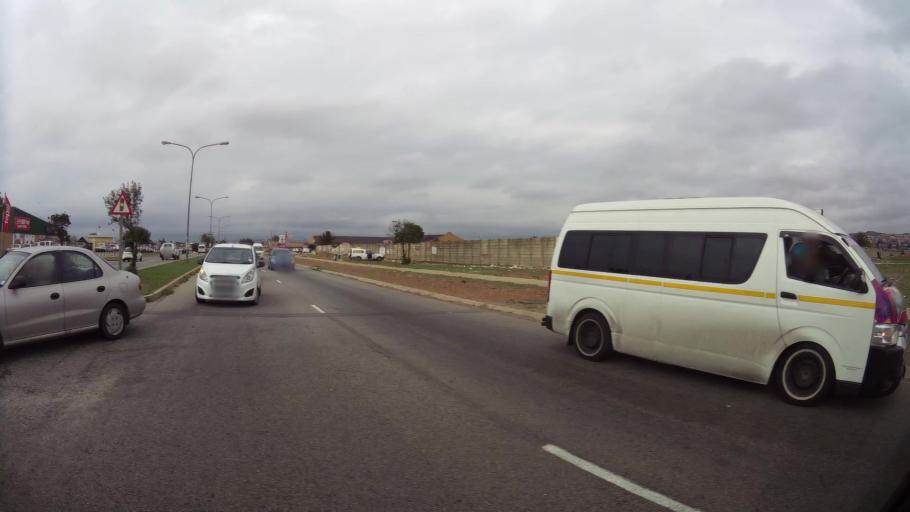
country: ZA
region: Eastern Cape
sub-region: Nelson Mandela Bay Metropolitan Municipality
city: Port Elizabeth
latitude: -33.9019
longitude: 25.5607
